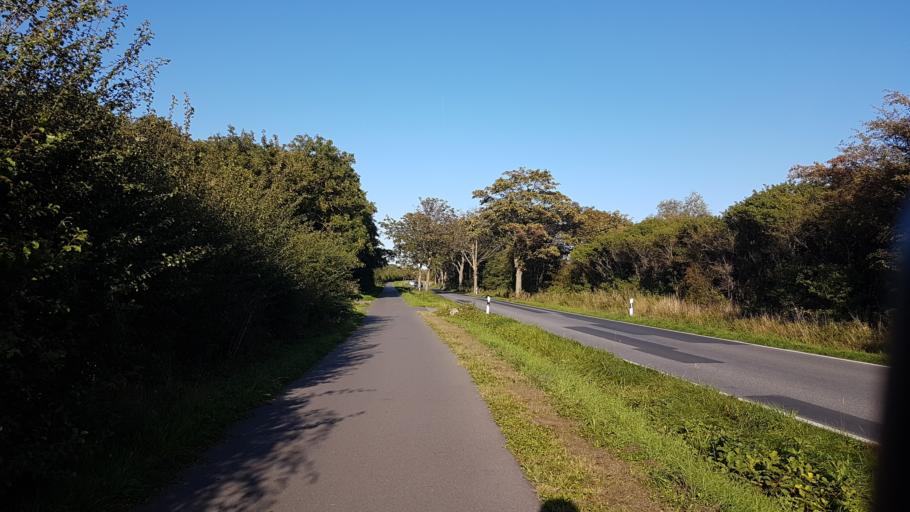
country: DE
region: Mecklenburg-Vorpommern
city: Dranske
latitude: 54.6399
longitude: 13.2555
